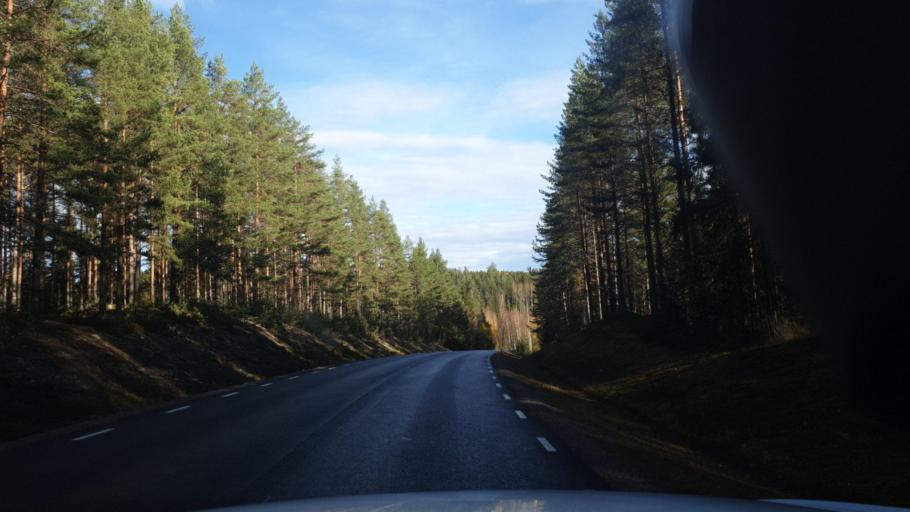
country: SE
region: Vaermland
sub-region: Arvika Kommun
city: Arvika
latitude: 59.9163
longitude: 12.6489
